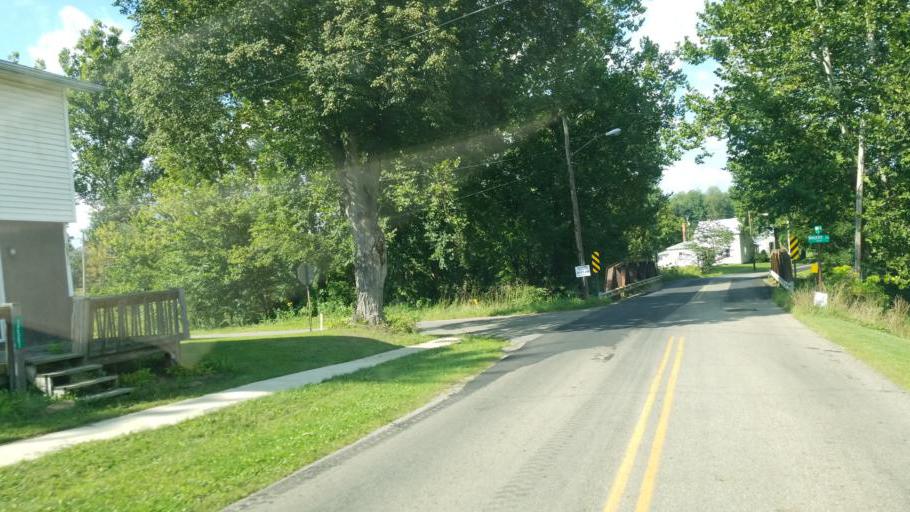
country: US
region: Ohio
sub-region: Knox County
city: Danville
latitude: 40.4122
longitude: -82.3243
